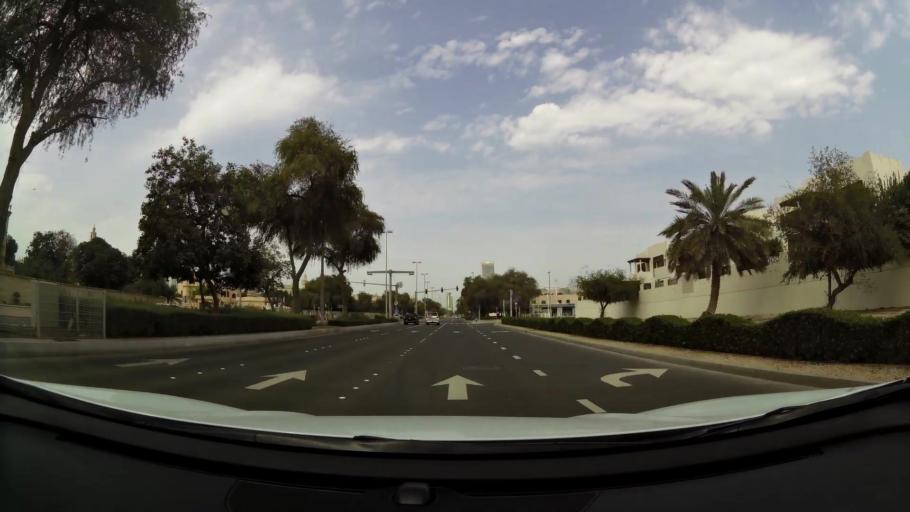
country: AE
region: Abu Dhabi
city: Abu Dhabi
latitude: 24.4569
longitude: 54.3496
